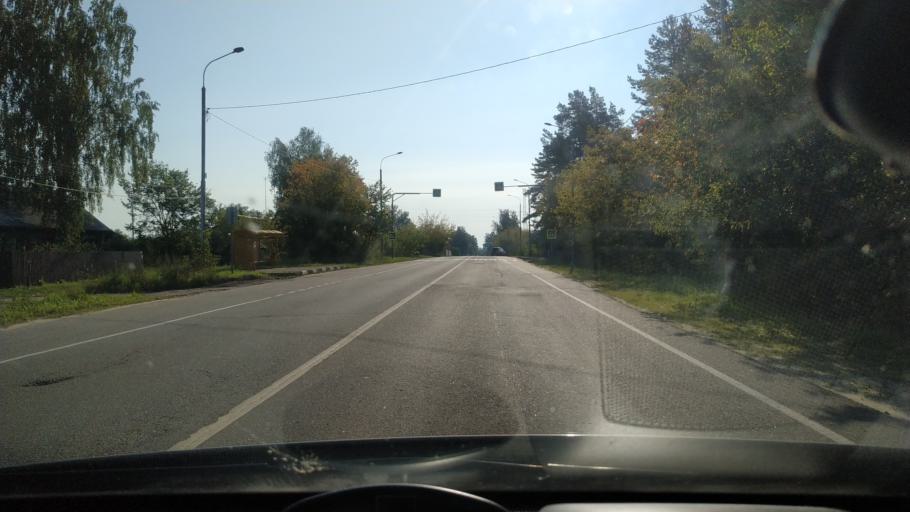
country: RU
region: Moskovskaya
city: Kerva
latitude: 55.5628
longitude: 39.6642
